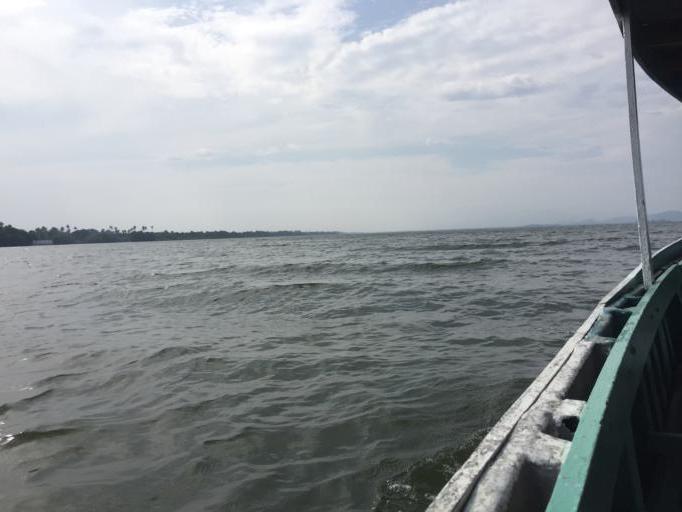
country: MX
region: Guerrero
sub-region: Coyuca de Benitez
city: Colonia Luces en el Mar
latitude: 16.9145
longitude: -99.9797
